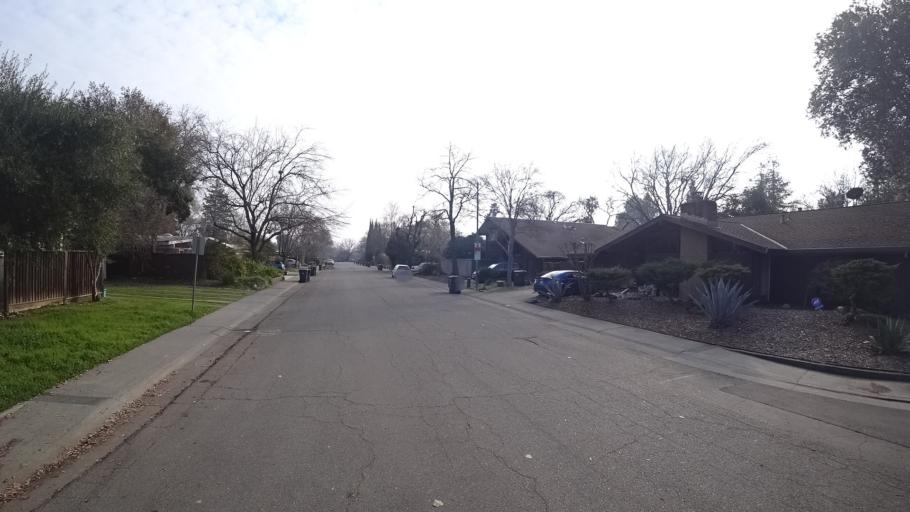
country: US
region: California
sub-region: Yolo County
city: Davis
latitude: 38.5549
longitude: -121.7648
